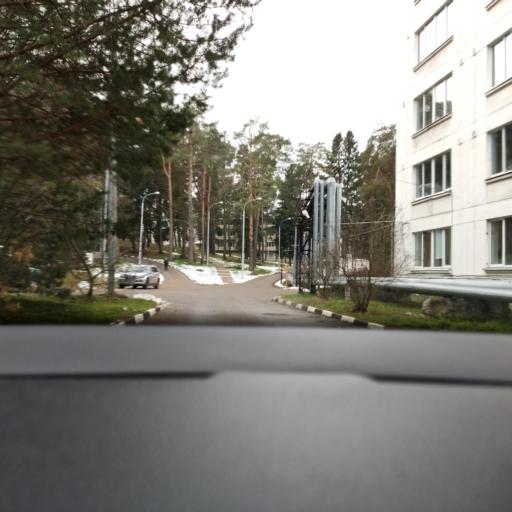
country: RU
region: Moskovskaya
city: Zvenigorod
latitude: 55.7135
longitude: 36.8916
